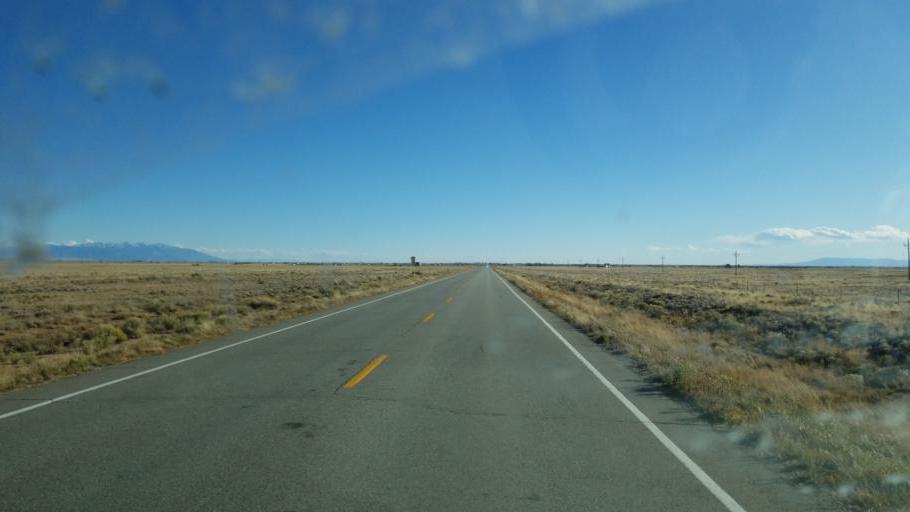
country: US
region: Colorado
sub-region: Saguache County
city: Saguache
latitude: 38.1621
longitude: -105.9266
